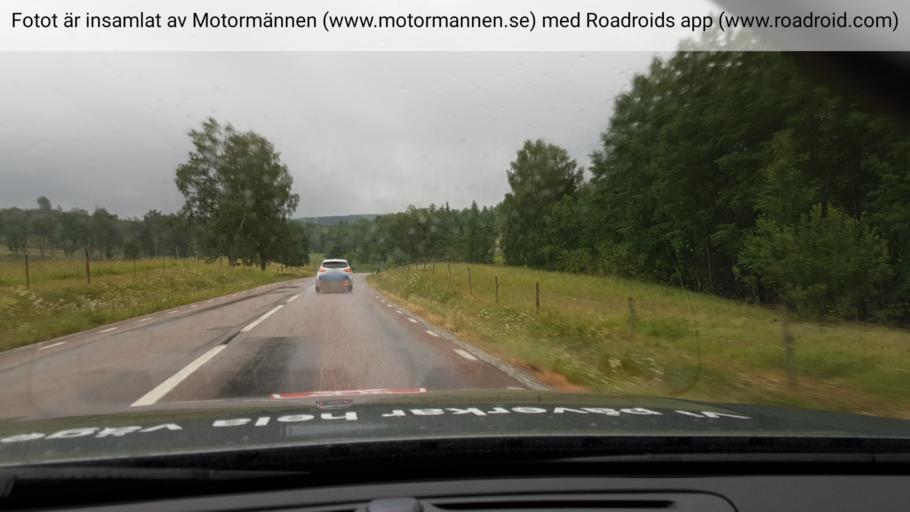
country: SE
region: Dalarna
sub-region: Avesta Kommun
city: Avesta
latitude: 59.9954
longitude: 16.1004
